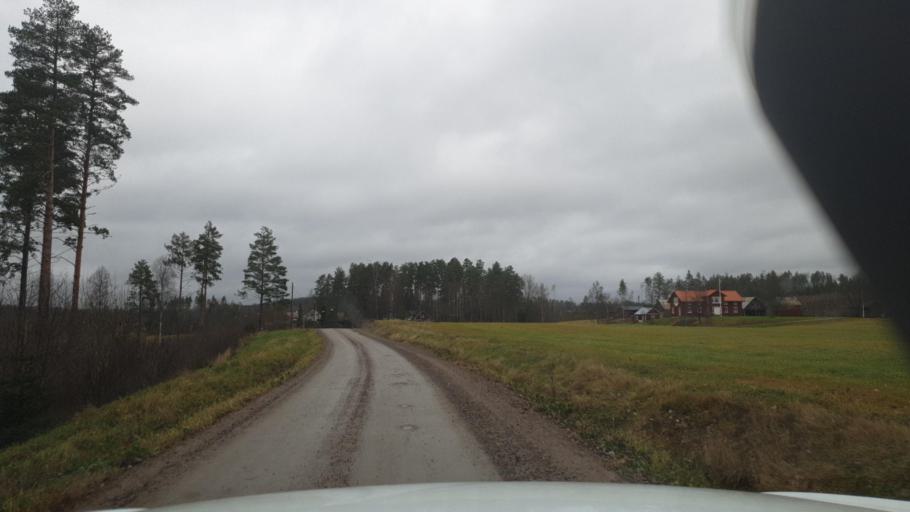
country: SE
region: Vaermland
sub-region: Arvika Kommun
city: Arvika
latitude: 59.8696
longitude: 12.6153
